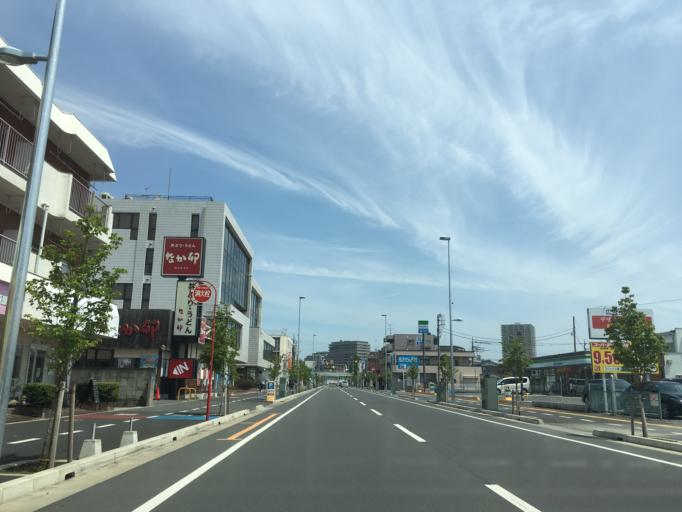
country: JP
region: Saitama
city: Ageoshimo
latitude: 35.9683
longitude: 139.5805
